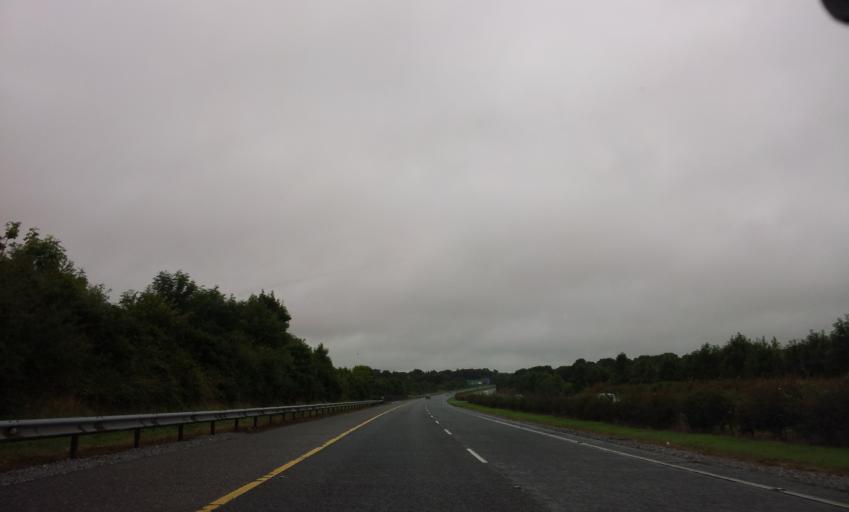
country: IE
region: Munster
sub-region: County Cork
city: Watergrasshill
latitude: 51.9867
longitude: -8.3636
